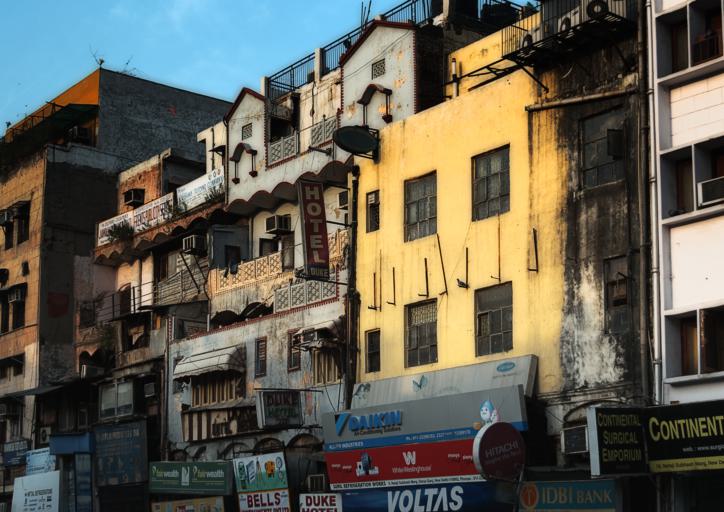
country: IN
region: NCT
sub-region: North Delhi
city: Delhi
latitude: 28.6472
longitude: 77.2403
